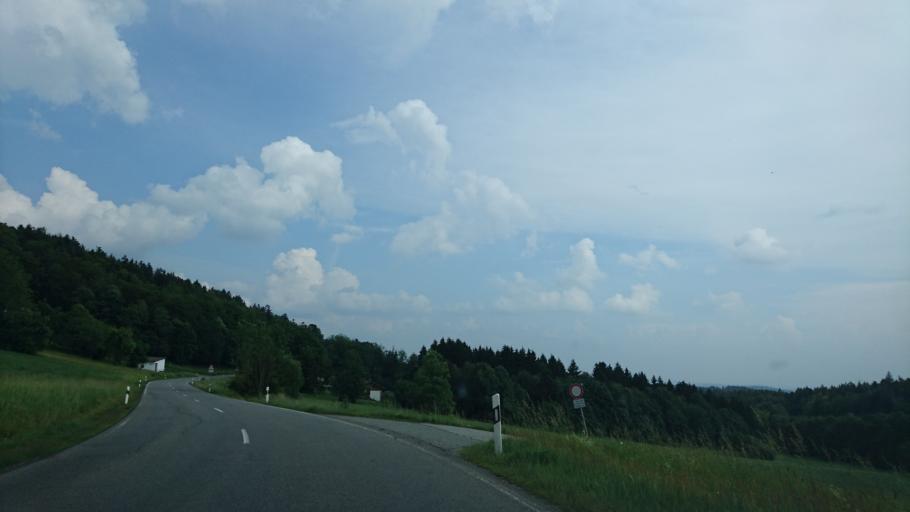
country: DE
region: Bavaria
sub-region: Lower Bavaria
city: Eppenschlag
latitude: 48.9190
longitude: 13.3227
